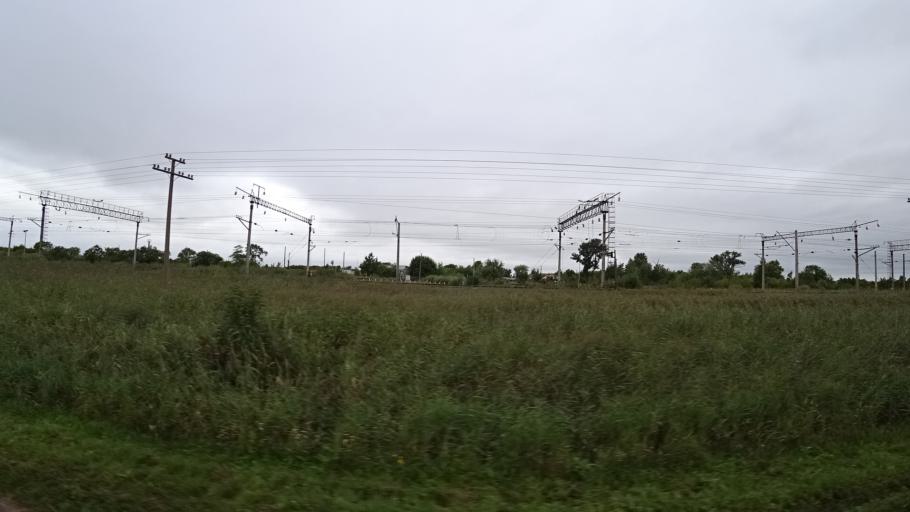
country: RU
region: Primorskiy
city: Chernigovka
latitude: 44.3350
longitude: 132.5270
